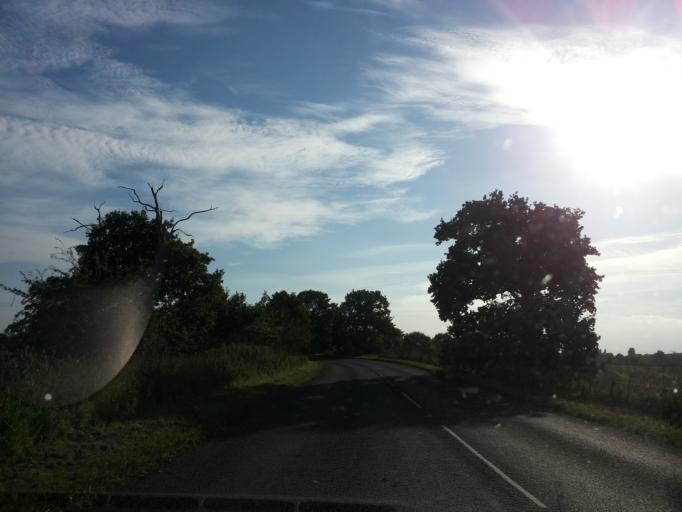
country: GB
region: England
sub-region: Doncaster
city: Hatfield
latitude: 53.6005
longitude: -0.9665
